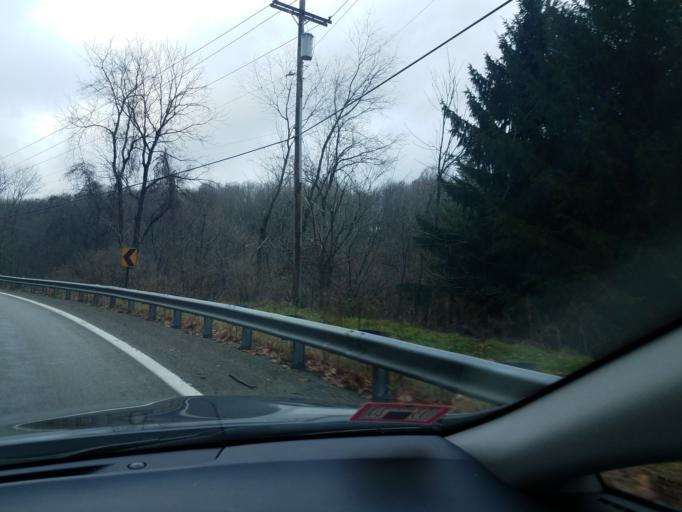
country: US
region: Pennsylvania
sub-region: Allegheny County
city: Franklin Park
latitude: 40.5648
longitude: -80.0613
